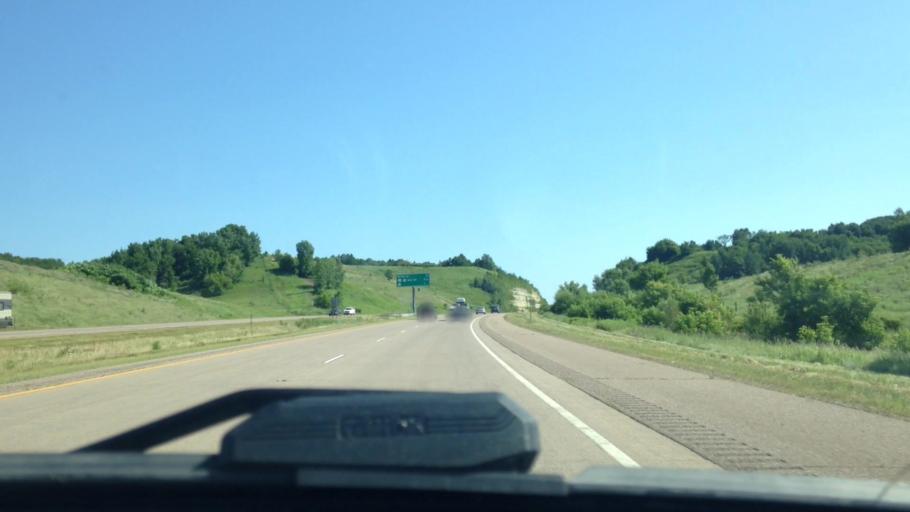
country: US
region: Wisconsin
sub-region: Eau Claire County
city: Seymour
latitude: 44.8474
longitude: -91.4391
